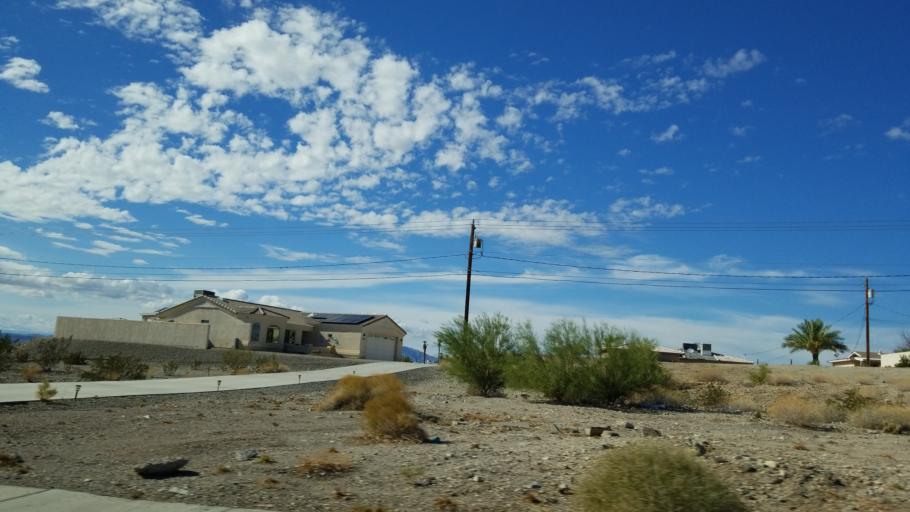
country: US
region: Arizona
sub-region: Mohave County
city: Lake Havasu City
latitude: 34.4802
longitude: -114.3168
